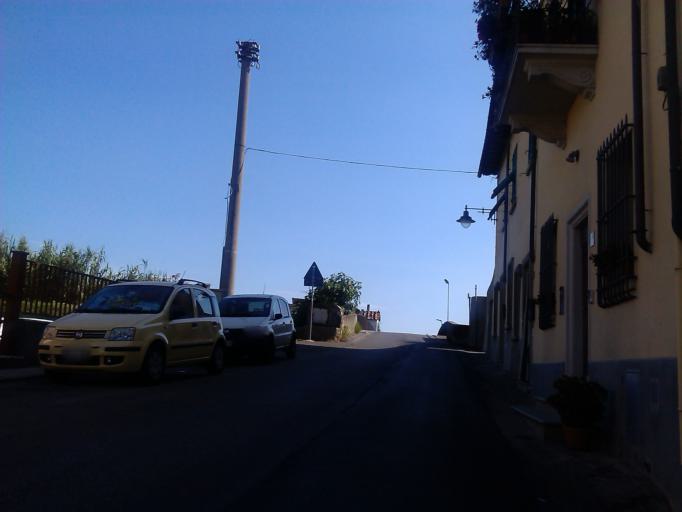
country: IT
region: Tuscany
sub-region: Province of Florence
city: Campi Bisenzio
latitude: 43.8392
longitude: 11.1326
